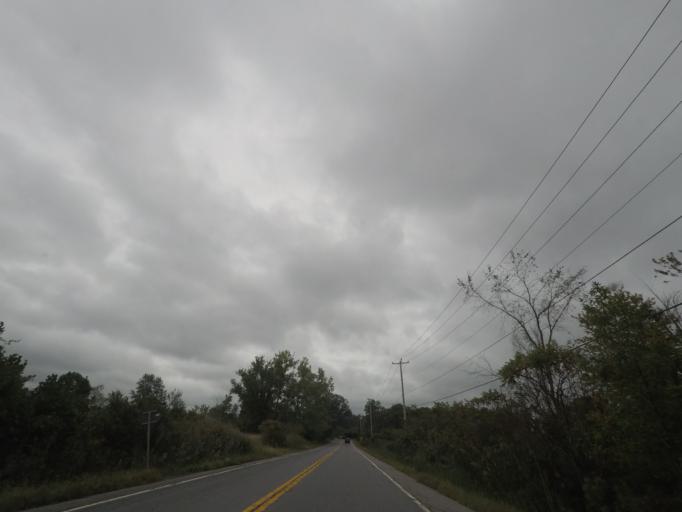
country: US
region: New York
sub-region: Saratoga County
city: Country Knolls
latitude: 42.9344
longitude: -73.7683
